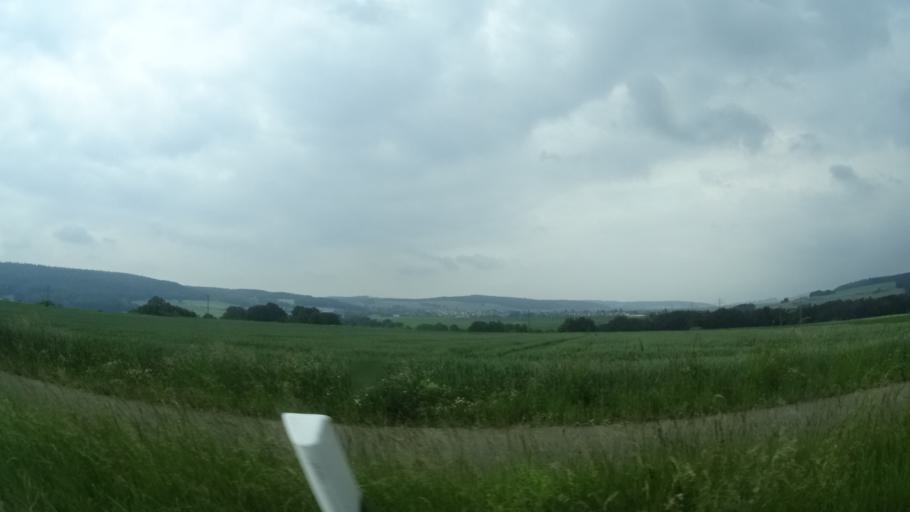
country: DE
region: Hesse
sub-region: Regierungsbezirk Kassel
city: Bad Salzschlirf
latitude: 50.6061
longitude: 9.5076
